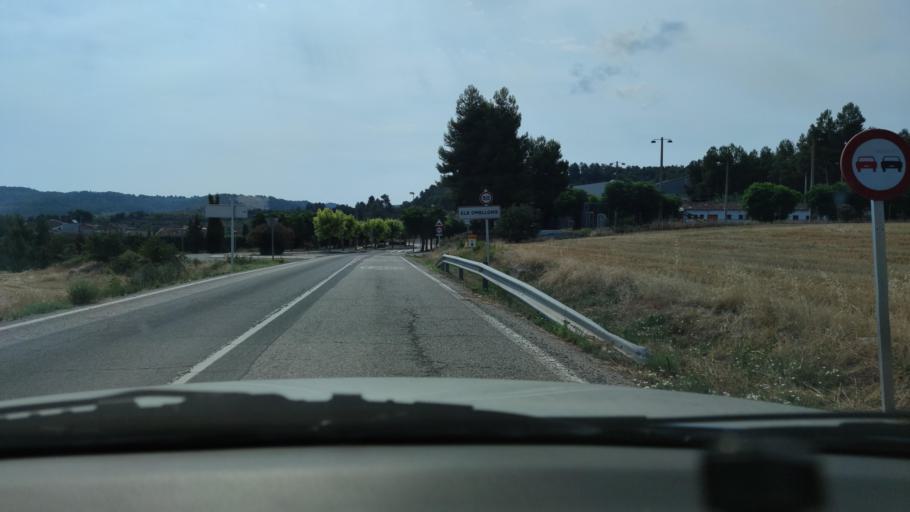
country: ES
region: Catalonia
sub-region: Provincia de Lleida
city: Arbeca
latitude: 41.5007
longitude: 0.9553
